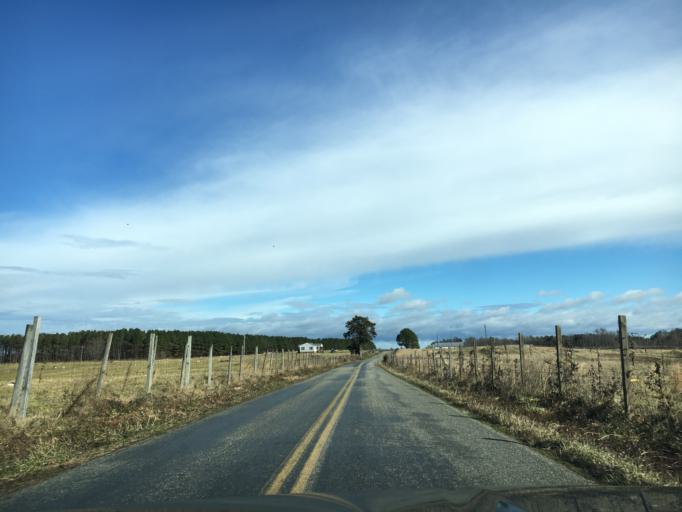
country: US
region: Virginia
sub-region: Amelia County
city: Amelia Court House
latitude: 37.4161
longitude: -78.0797
